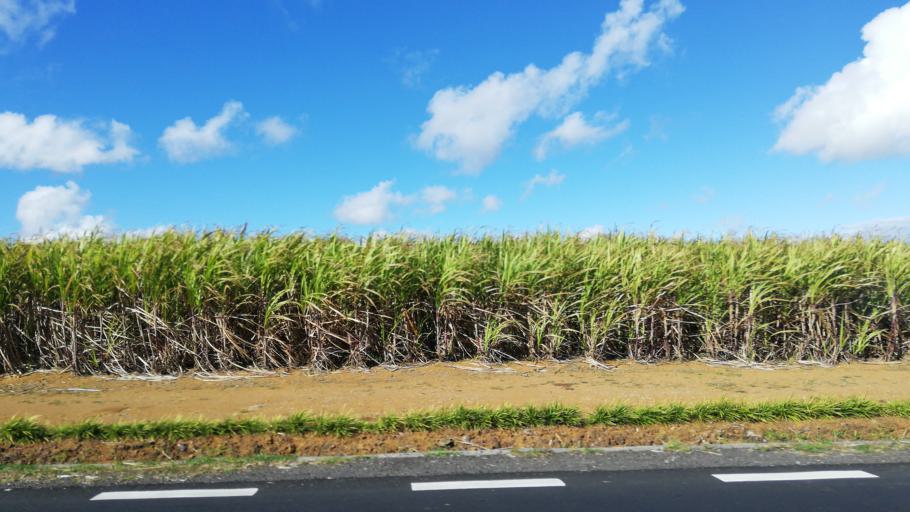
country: MU
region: Moka
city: La Dagotiere
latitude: -20.2337
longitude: 57.5662
